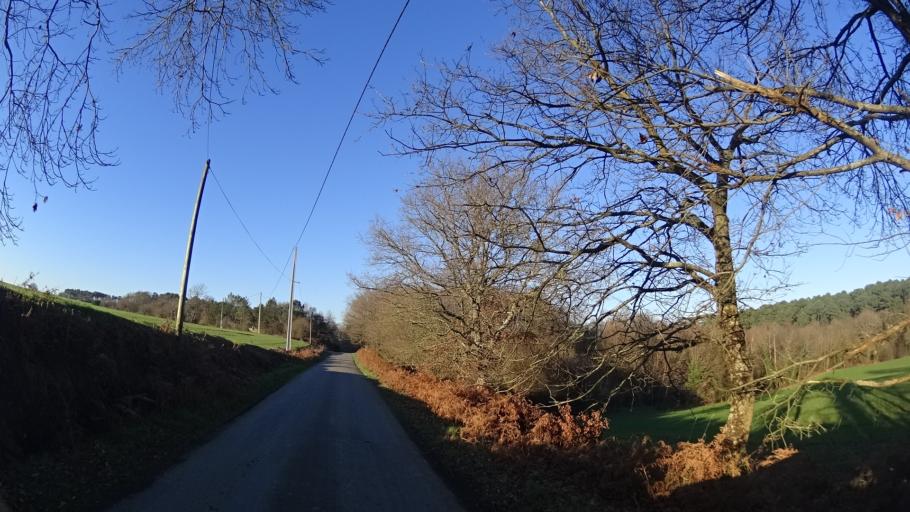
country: FR
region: Brittany
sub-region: Departement du Morbihan
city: Allaire
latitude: 47.6553
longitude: -2.1583
